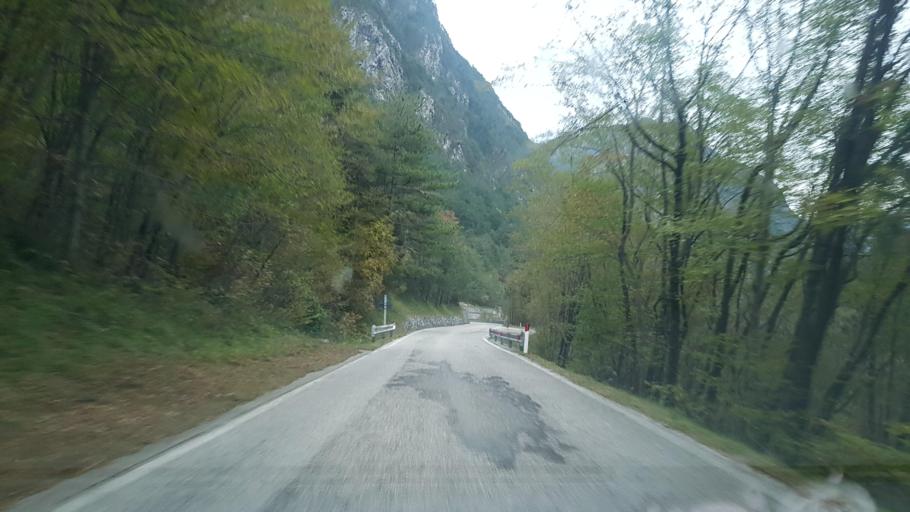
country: IT
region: Friuli Venezia Giulia
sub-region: Provincia di Udine
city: Villa Santina
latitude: 46.3422
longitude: 12.9261
